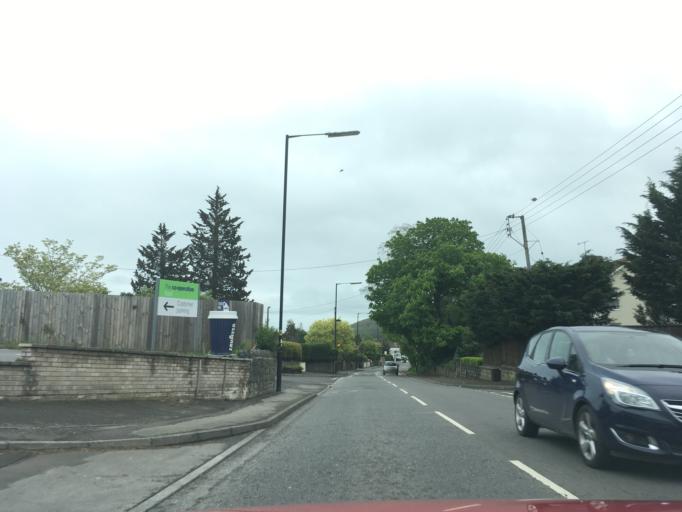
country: GB
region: England
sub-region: North Somerset
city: Banwell
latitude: 51.3298
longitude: -2.8760
